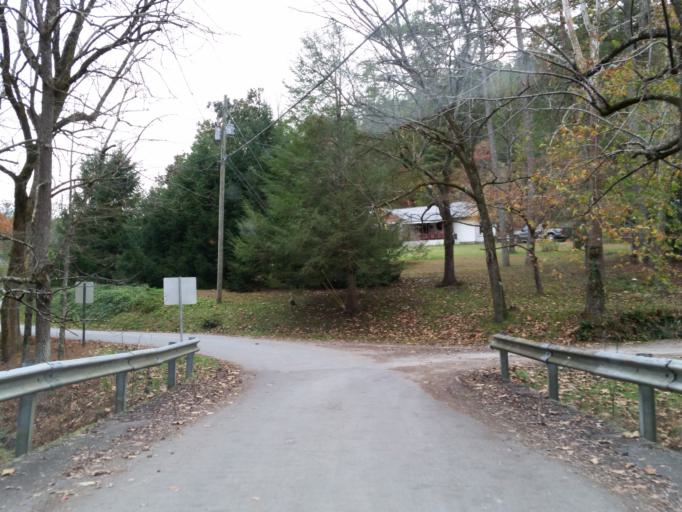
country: US
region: Georgia
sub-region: Gilmer County
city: Ellijay
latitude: 34.6420
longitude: -84.3015
